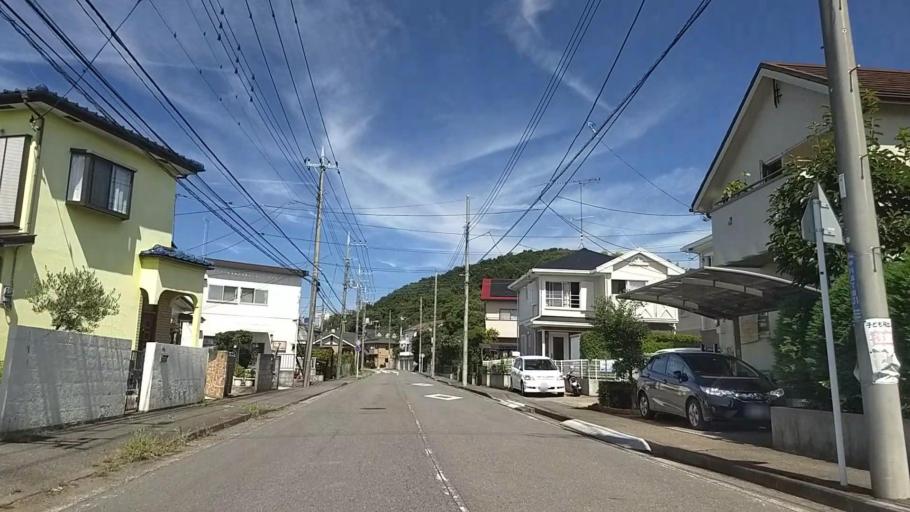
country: JP
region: Tokyo
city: Chofugaoka
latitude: 35.5557
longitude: 139.5693
